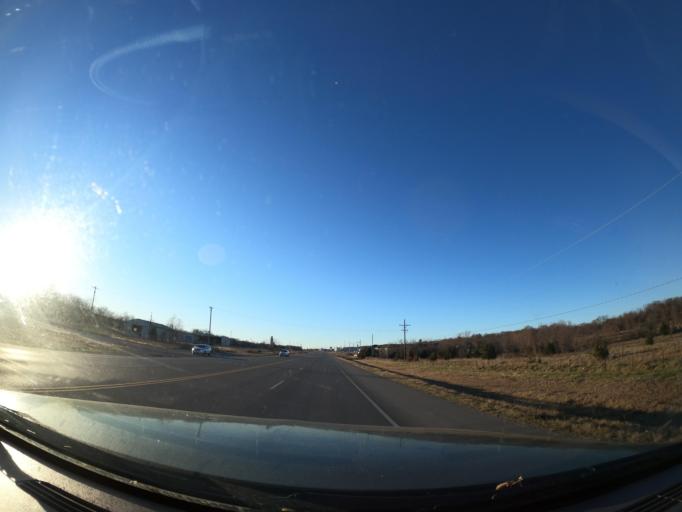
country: US
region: Oklahoma
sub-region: Pittsburg County
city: Krebs
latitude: 34.8954
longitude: -95.6702
